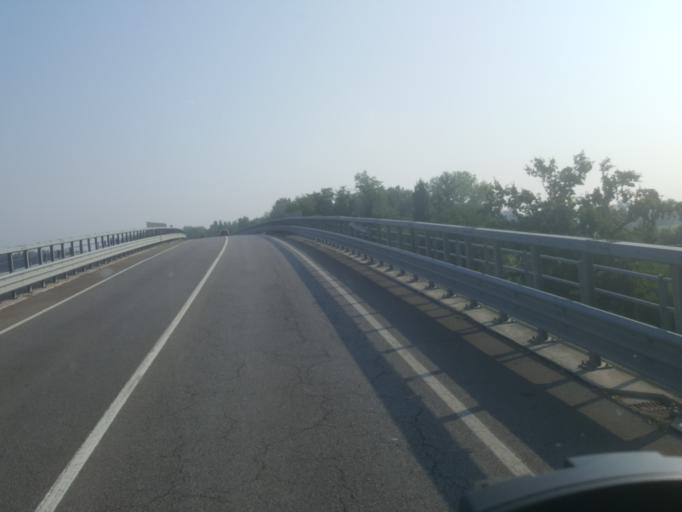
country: IT
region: Emilia-Romagna
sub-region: Provincia di Ravenna
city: Alfonsine
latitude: 44.4981
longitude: 12.0579
